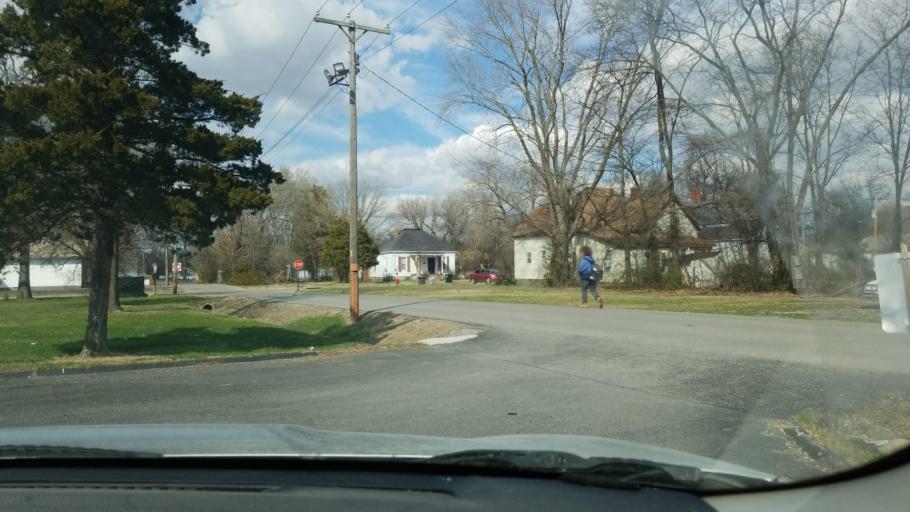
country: US
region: Illinois
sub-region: Saline County
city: Harrisburg
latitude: 37.7366
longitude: -88.5497
